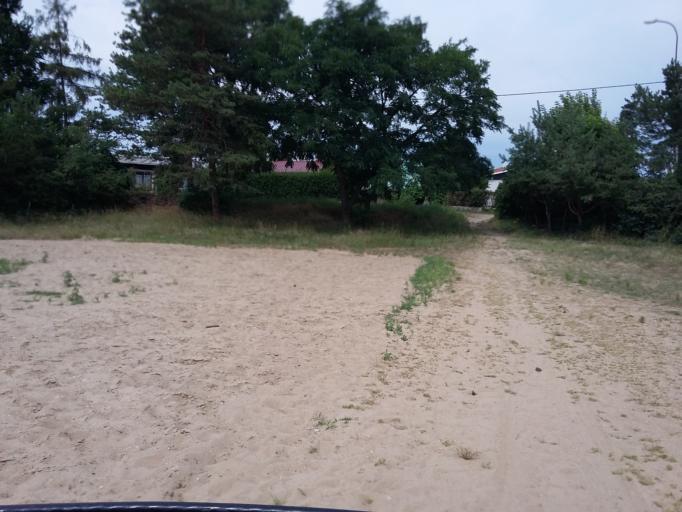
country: AT
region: Lower Austria
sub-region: Politischer Bezirk Ganserndorf
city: Drosing
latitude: 48.4926
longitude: 16.9559
